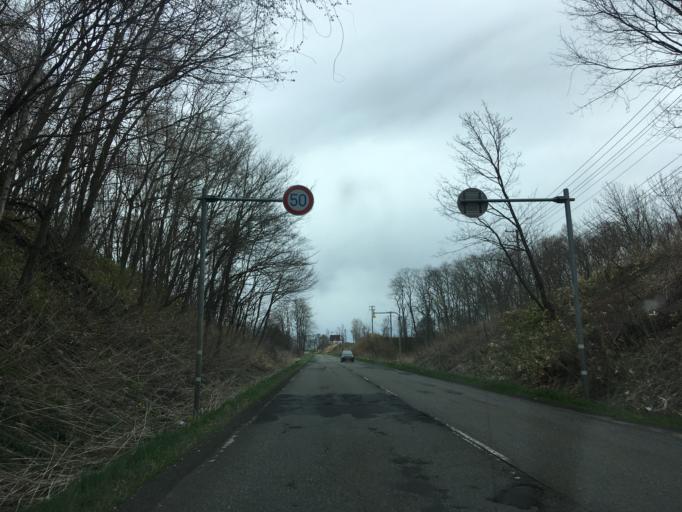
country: JP
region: Hokkaido
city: Chitose
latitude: 42.8950
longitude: 141.8134
